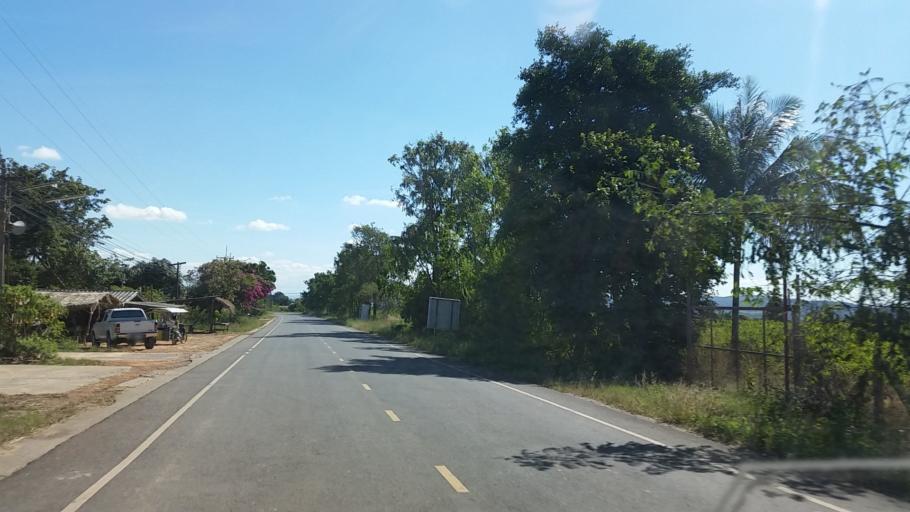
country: TH
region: Chaiyaphum
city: Sap Yai
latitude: 15.6128
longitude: 101.4026
